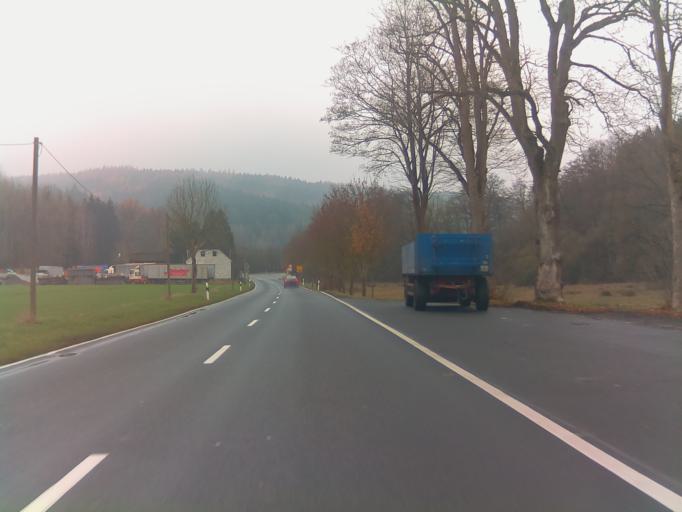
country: DE
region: Thuringia
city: Ahlstadt
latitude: 50.4894
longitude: 10.6961
